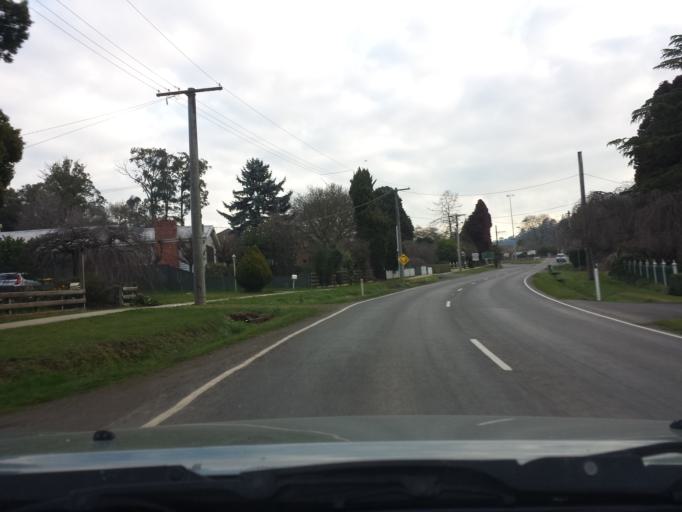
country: AU
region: Victoria
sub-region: Yarra Ranges
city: Monbulk
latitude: -37.8725
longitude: 145.4075
